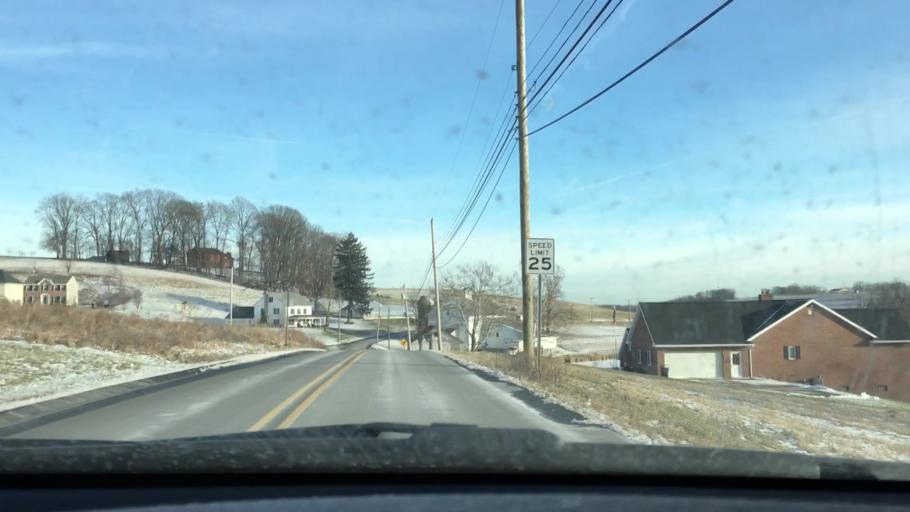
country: US
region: Pennsylvania
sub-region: Washington County
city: McMurray
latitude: 40.2814
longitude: -80.0388
